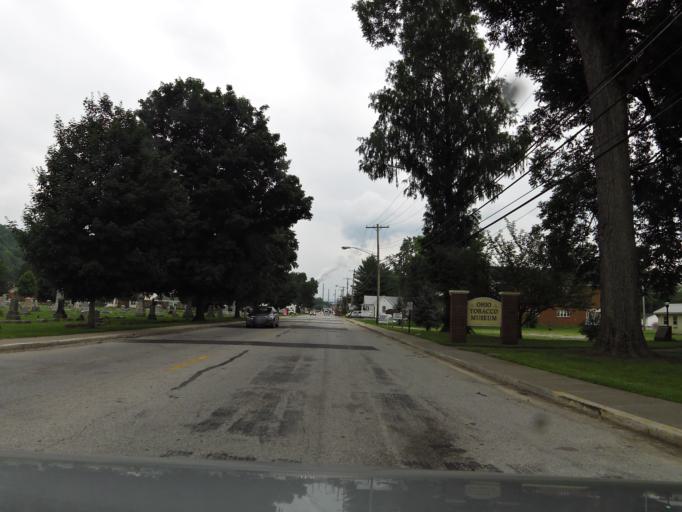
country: US
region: Ohio
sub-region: Brown County
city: Ripley
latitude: 38.7349
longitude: -83.8389
